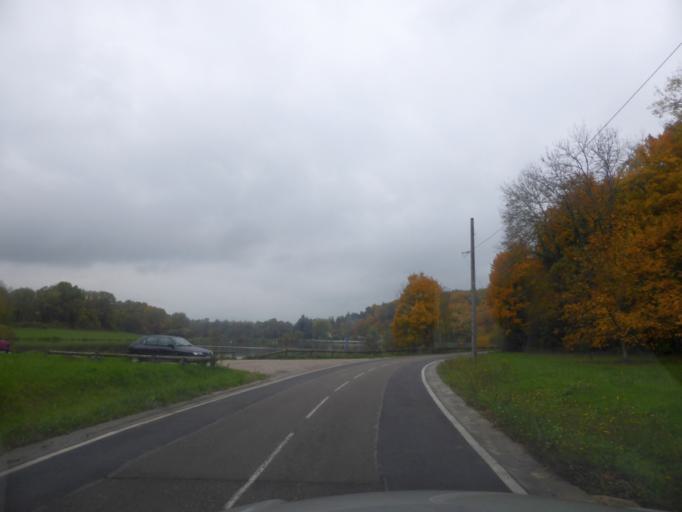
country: FR
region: Lorraine
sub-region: Departement de Meurthe-et-Moselle
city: Villey-Saint-Etienne
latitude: 48.7463
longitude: 6.0054
